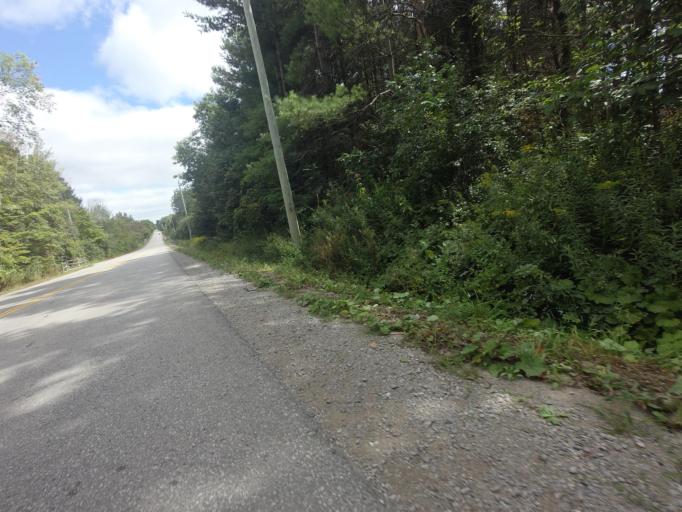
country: CA
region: Ontario
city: Uxbridge
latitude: 44.1232
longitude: -79.1766
